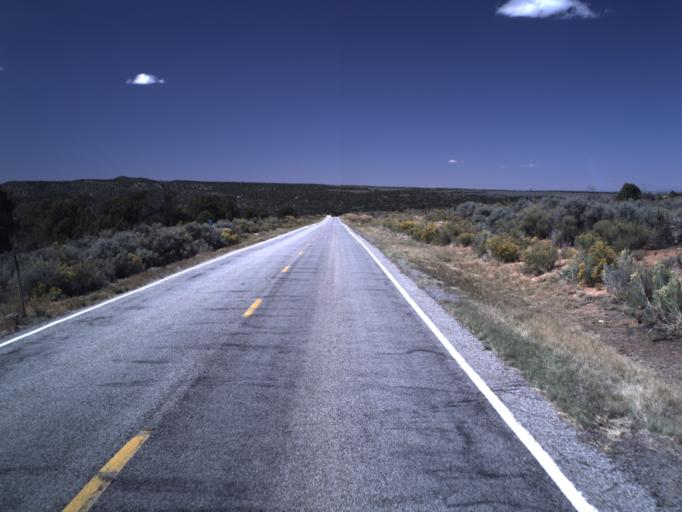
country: US
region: Utah
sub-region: Grand County
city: Moab
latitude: 38.3176
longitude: -109.3188
